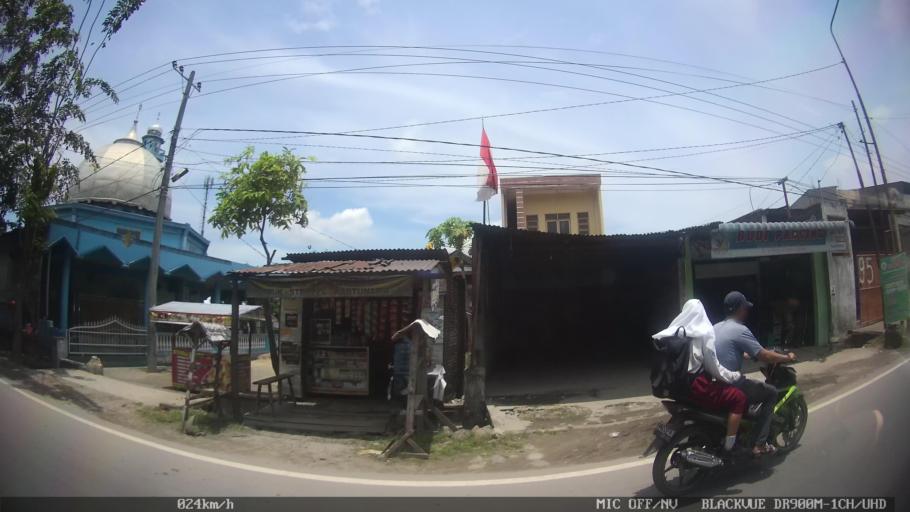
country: ID
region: North Sumatra
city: Labuhan Deli
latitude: 3.7188
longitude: 98.6653
